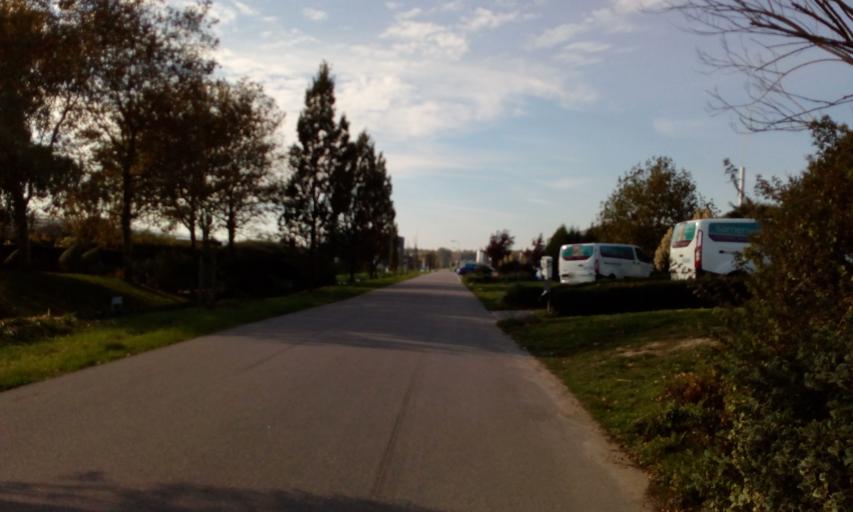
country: NL
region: South Holland
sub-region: Gemeente Westland
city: De Lier
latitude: 51.9780
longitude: 4.2841
